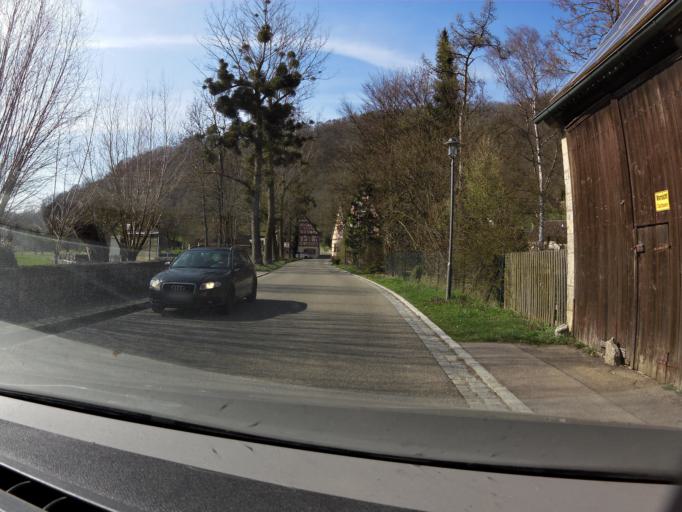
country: DE
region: Bavaria
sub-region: Regierungsbezirk Mittelfranken
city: Adelshofen
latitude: 49.4477
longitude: 10.1132
